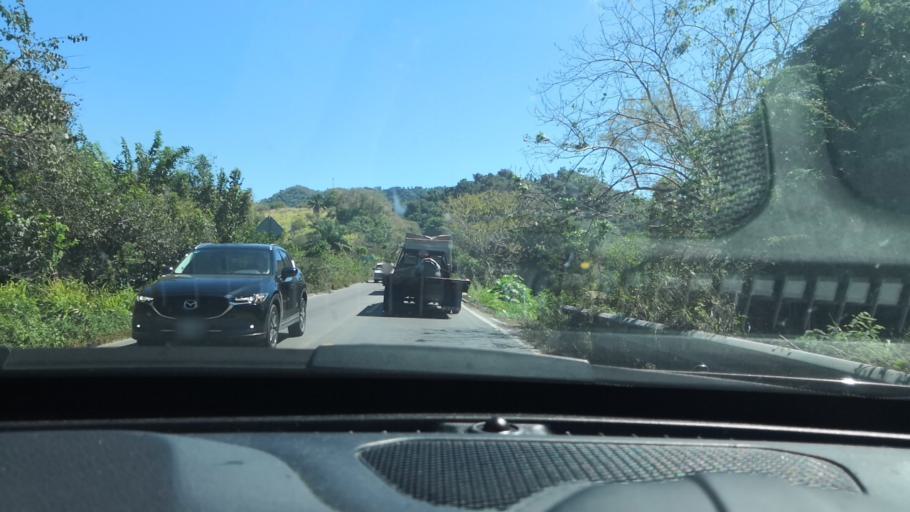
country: MX
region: Nayarit
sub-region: Bahia de Banderas
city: Lo de Marcos
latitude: 20.8953
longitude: -105.4015
